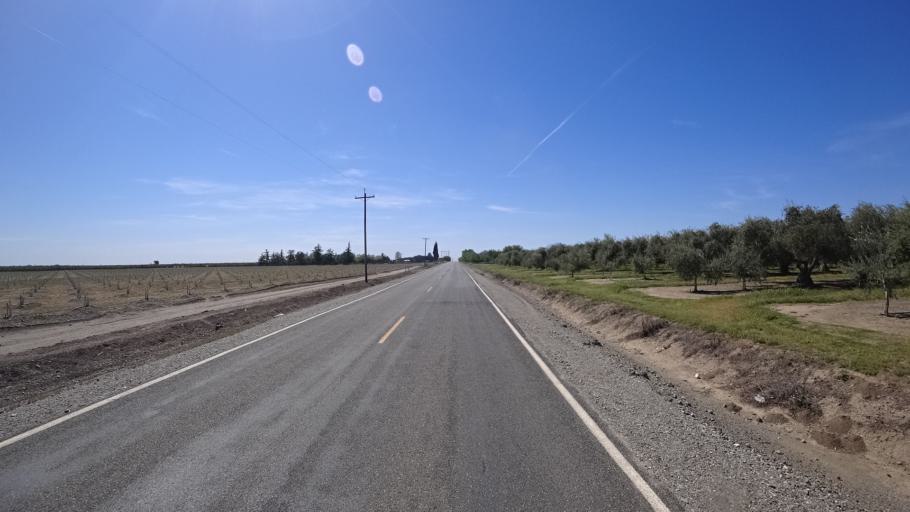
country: US
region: California
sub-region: Glenn County
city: Orland
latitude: 39.7084
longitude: -122.1409
